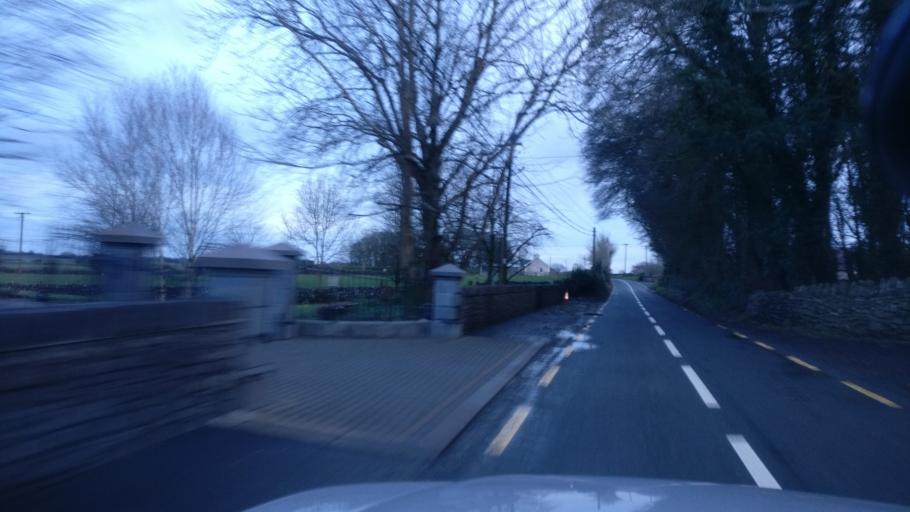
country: IE
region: Connaught
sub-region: County Galway
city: Athenry
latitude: 53.2543
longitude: -8.6768
